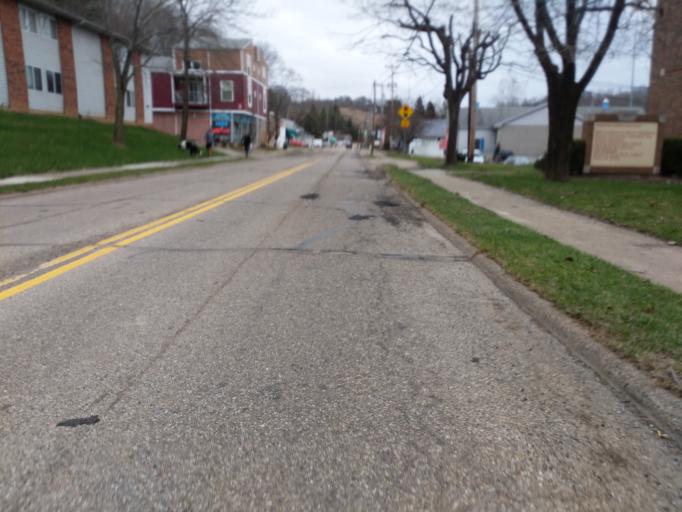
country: US
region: Ohio
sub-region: Athens County
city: Athens
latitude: 39.3067
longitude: -82.1040
